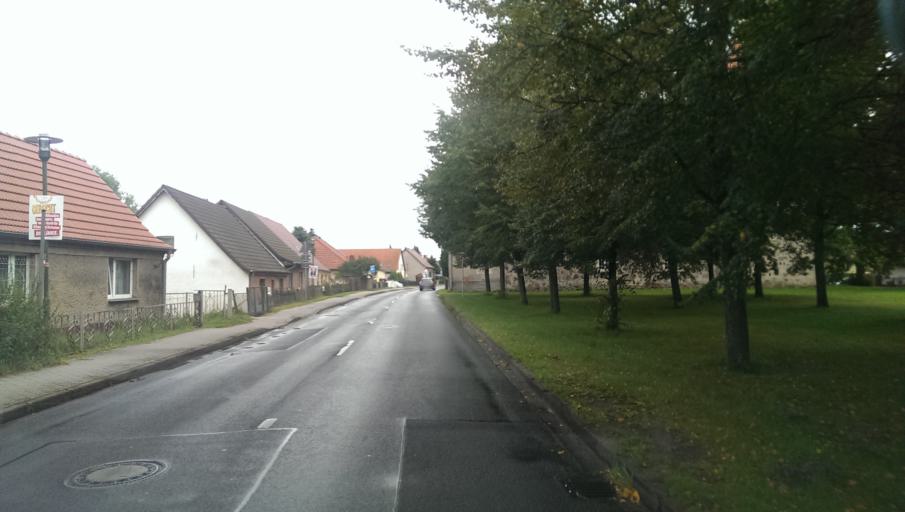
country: DE
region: Brandenburg
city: Velten
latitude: 52.6975
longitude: 13.1109
